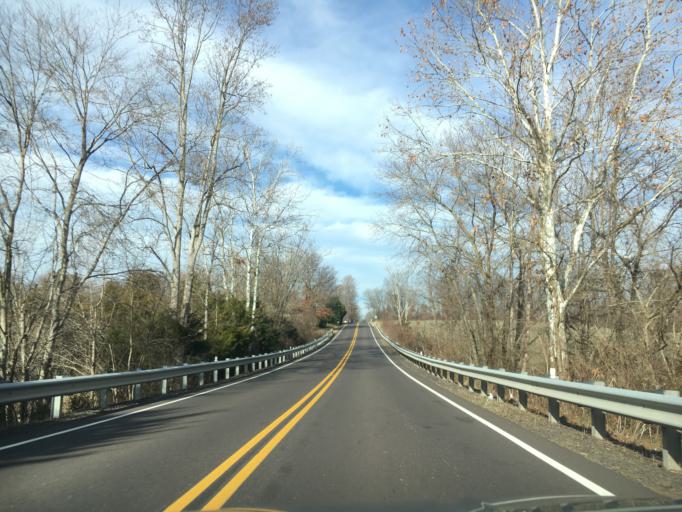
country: US
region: Virginia
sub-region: Louisa County
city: Louisa
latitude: 38.1259
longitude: -77.9152
